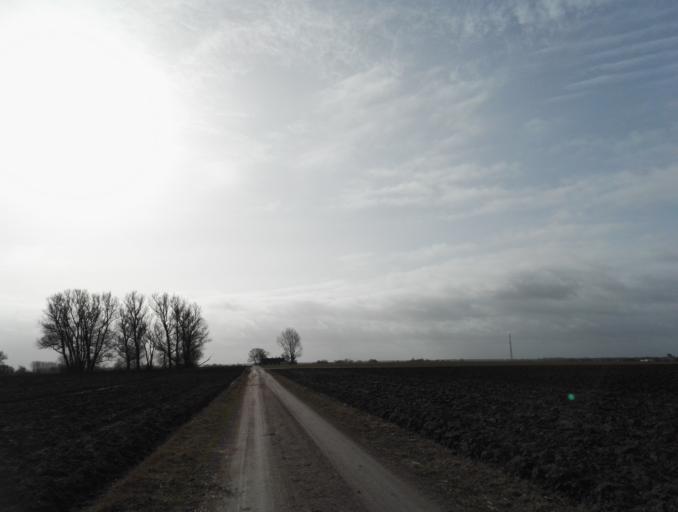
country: SE
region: Skane
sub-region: Landskrona
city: Asmundtorp
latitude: 55.8936
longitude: 13.0085
